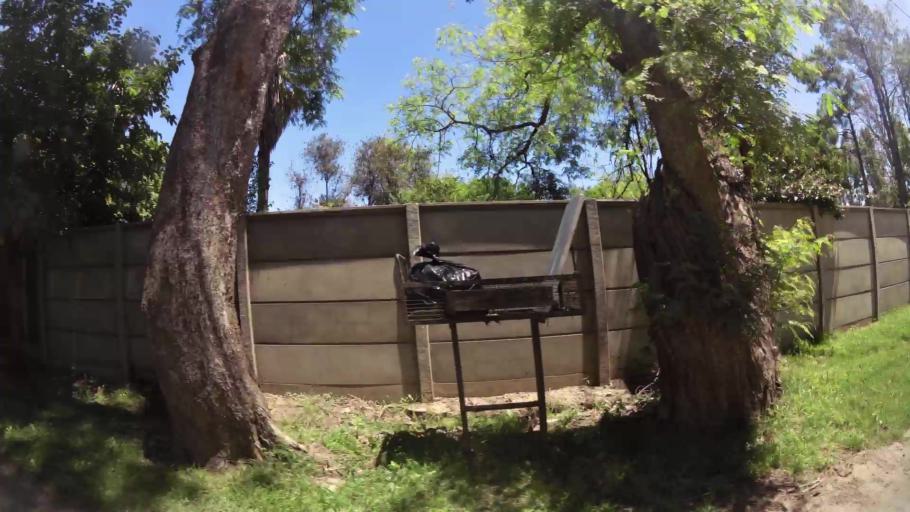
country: AR
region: Santa Fe
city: Rafaela
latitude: -31.2583
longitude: -61.4556
